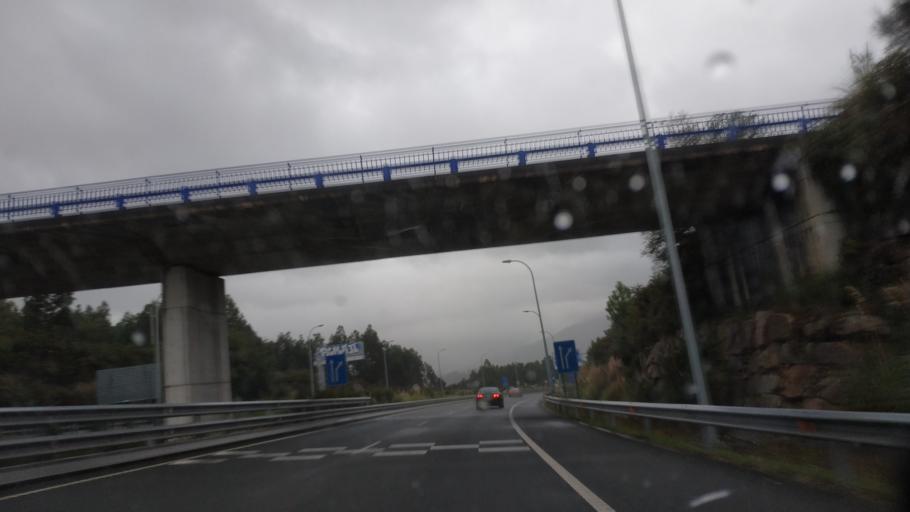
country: ES
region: Galicia
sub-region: Provincia da Coruna
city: Culleredo
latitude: 43.2784
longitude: -8.3950
